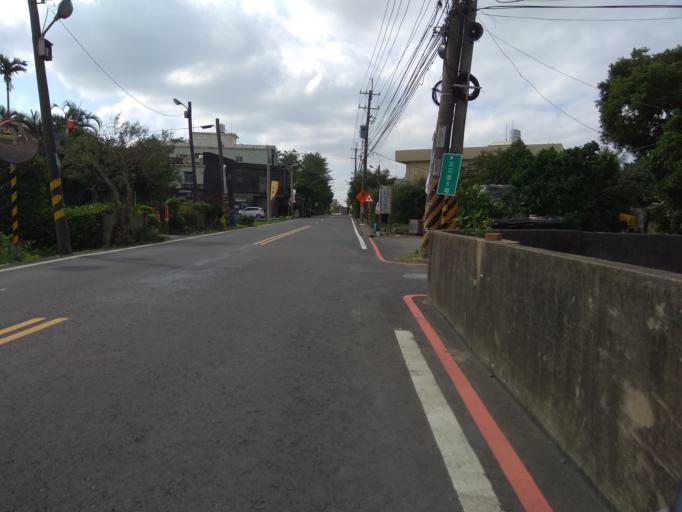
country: TW
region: Taiwan
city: Taoyuan City
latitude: 25.0657
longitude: 121.2406
